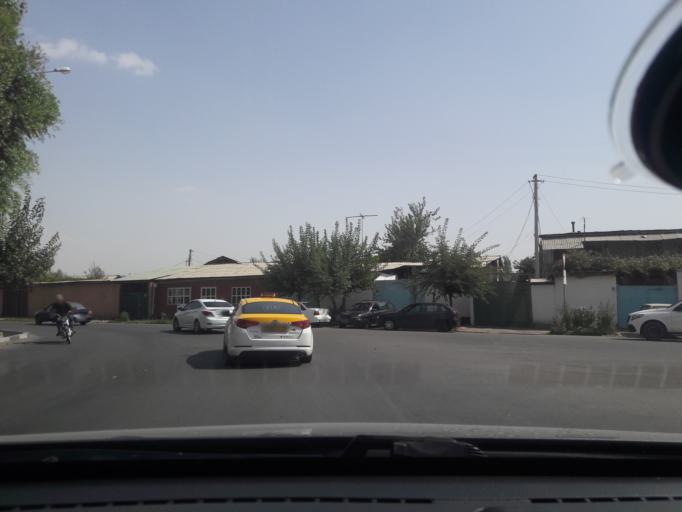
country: TJ
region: Dushanbe
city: Dushanbe
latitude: 38.5641
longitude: 68.7620
